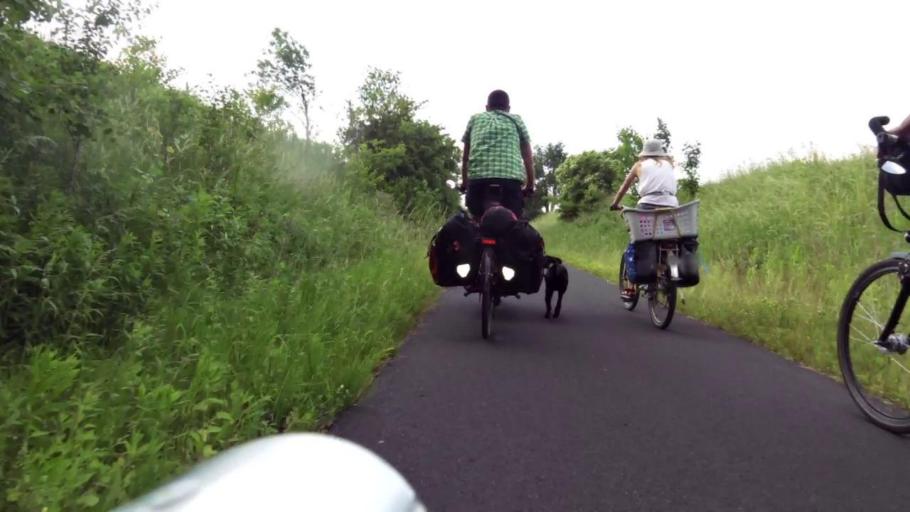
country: PL
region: Kujawsko-Pomorskie
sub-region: Powiat torunski
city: Lubianka
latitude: 53.0971
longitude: 18.5312
